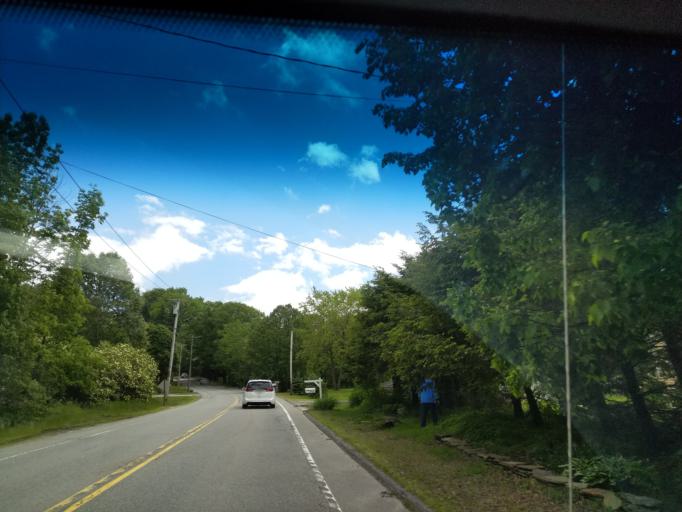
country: US
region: Maine
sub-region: Cumberland County
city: Falmouth
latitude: 43.7372
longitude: -70.2837
